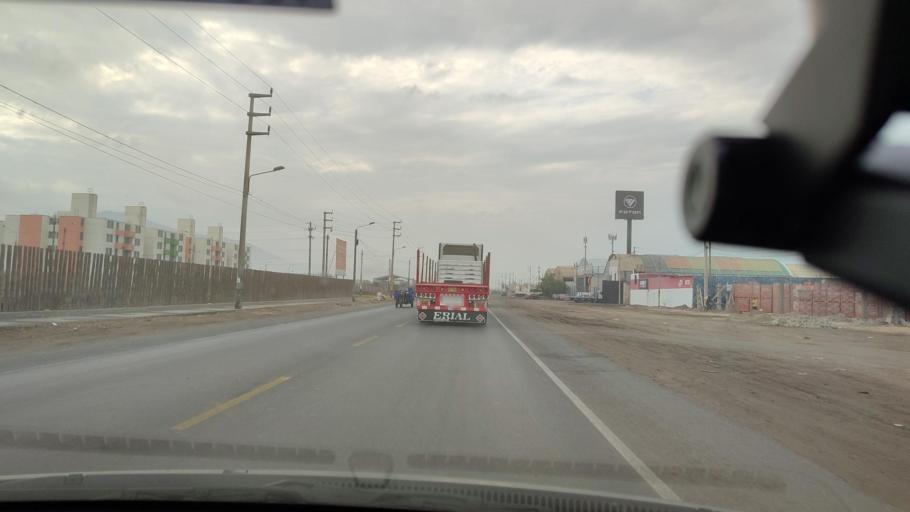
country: PE
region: La Libertad
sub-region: Provincia de Trujillo
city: Buenos Aires
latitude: -8.1463
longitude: -79.0459
